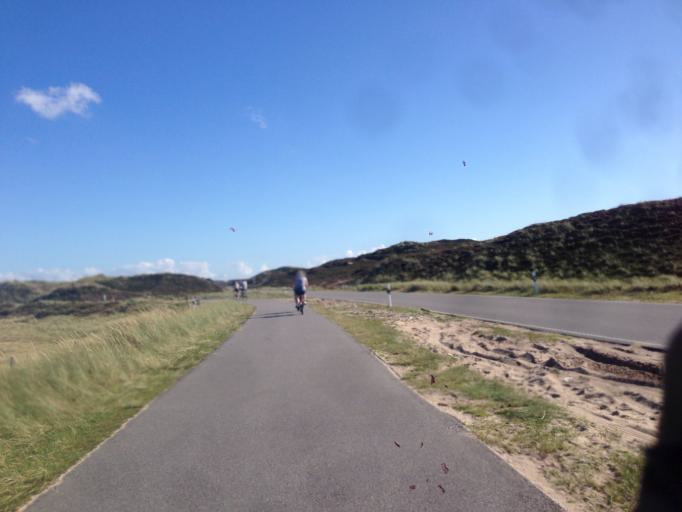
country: DE
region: Schleswig-Holstein
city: List
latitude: 55.0360
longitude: 8.3962
